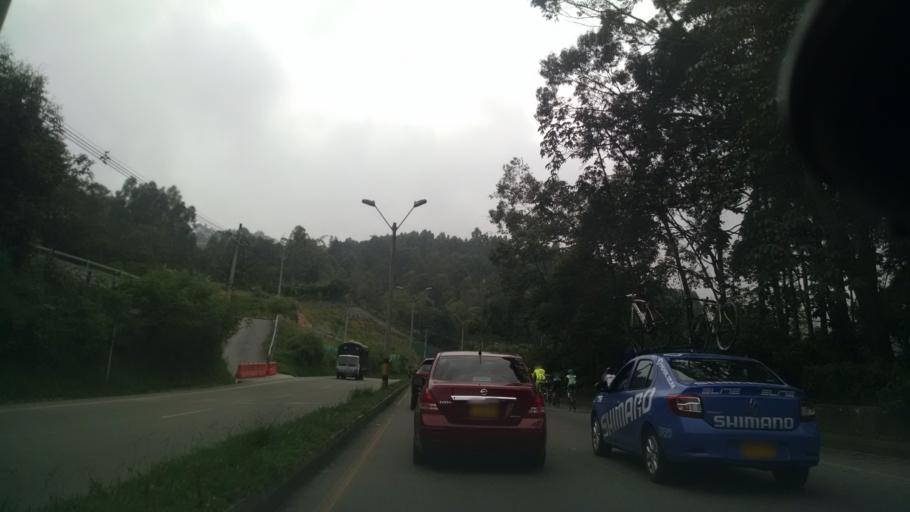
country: CO
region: Antioquia
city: Medellin
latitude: 6.2193
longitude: -75.5569
